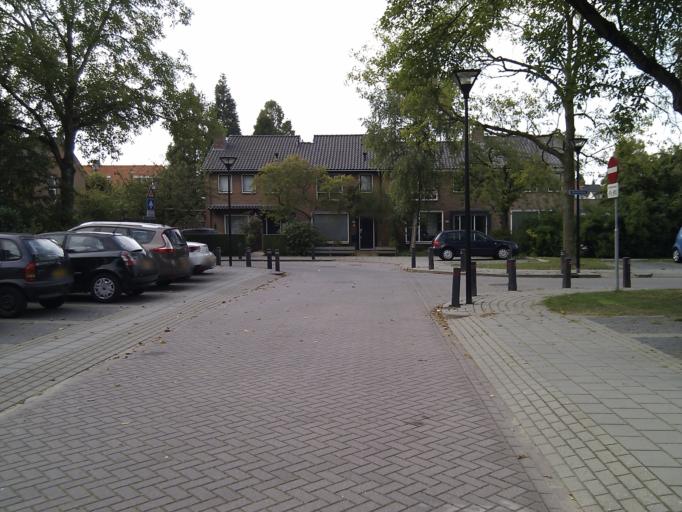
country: NL
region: Utrecht
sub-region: Gemeente De Bilt
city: De Bilt
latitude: 52.1129
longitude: 5.1813
